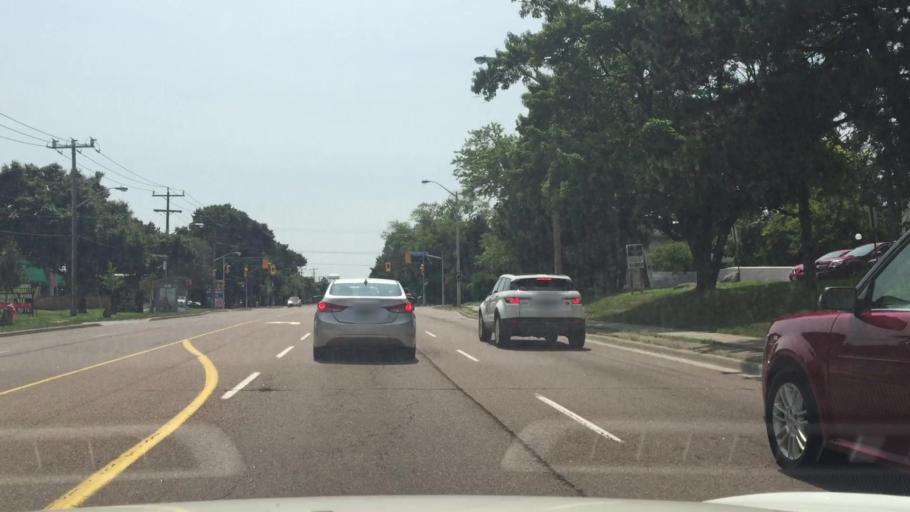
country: CA
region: Ontario
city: Willowdale
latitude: 43.7597
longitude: -79.3616
